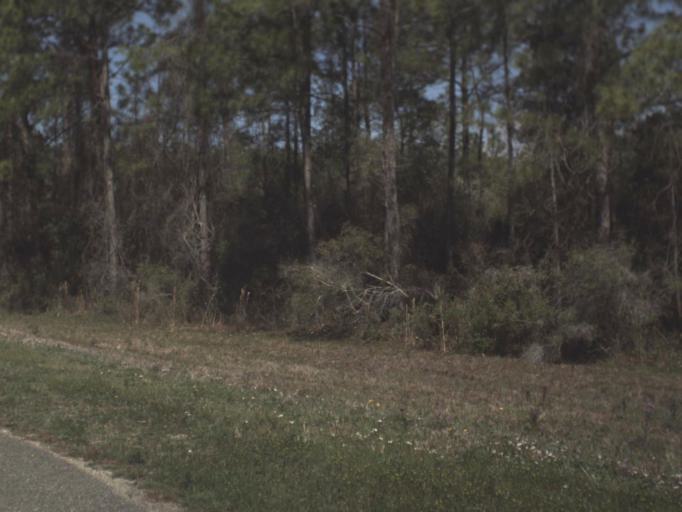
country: US
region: Florida
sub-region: Gulf County
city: Port Saint Joe
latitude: 29.7513
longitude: -85.2461
